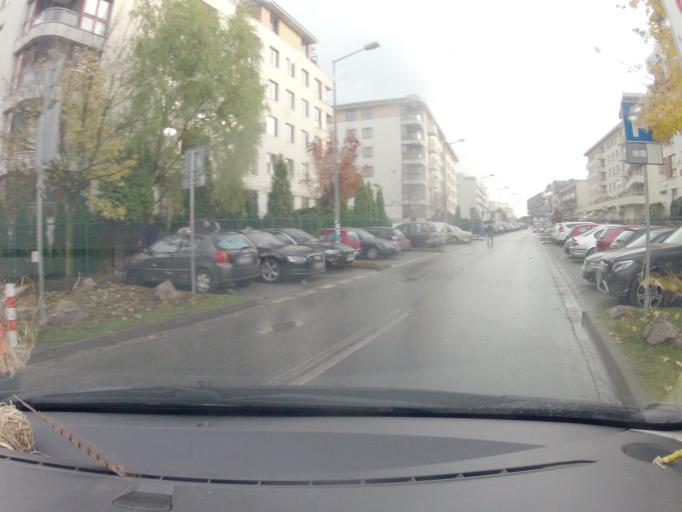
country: PL
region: Lesser Poland Voivodeship
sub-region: Krakow
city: Sidzina
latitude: 50.0156
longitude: 19.8896
